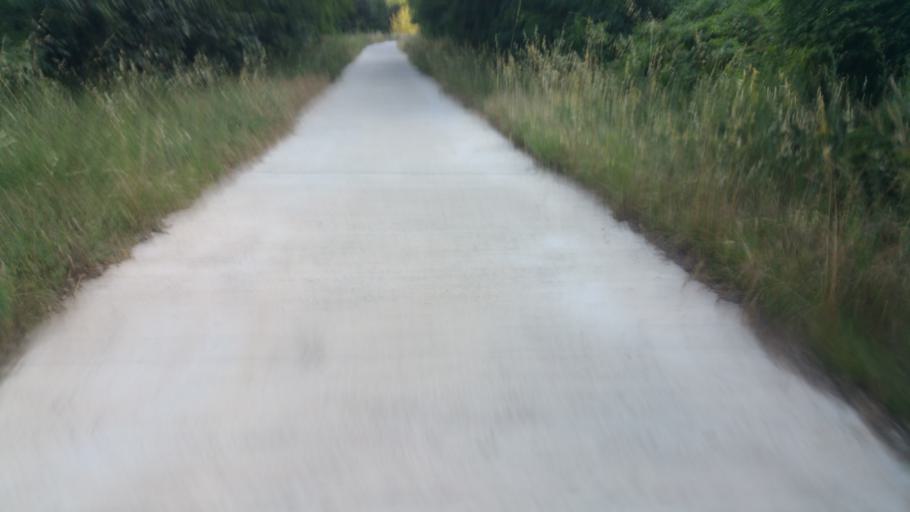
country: FR
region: Languedoc-Roussillon
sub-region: Departement des Pyrenees-Orientales
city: Reiners
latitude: 42.4866
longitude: 2.6982
